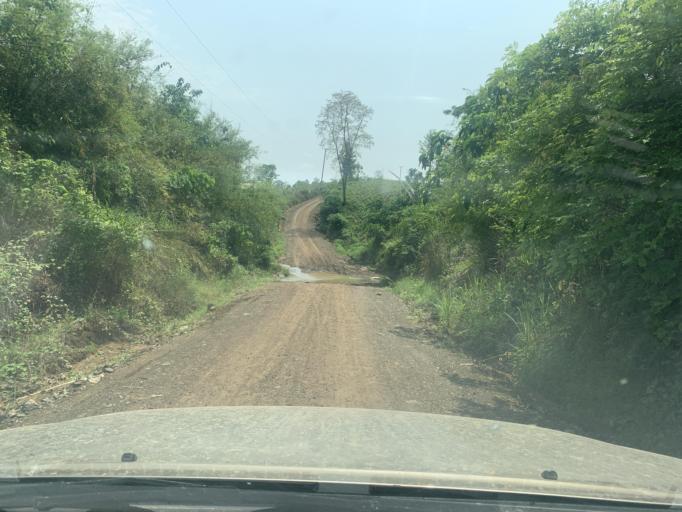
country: TH
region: Uttaradit
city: Ban Khok
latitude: 18.3563
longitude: 101.3817
